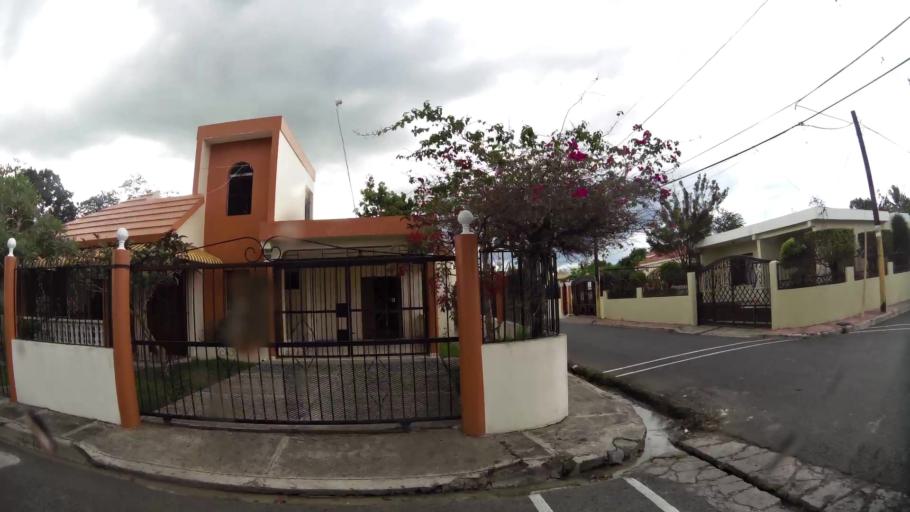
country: DO
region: Monsenor Nouel
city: Bonao
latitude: 18.9505
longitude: -70.4061
